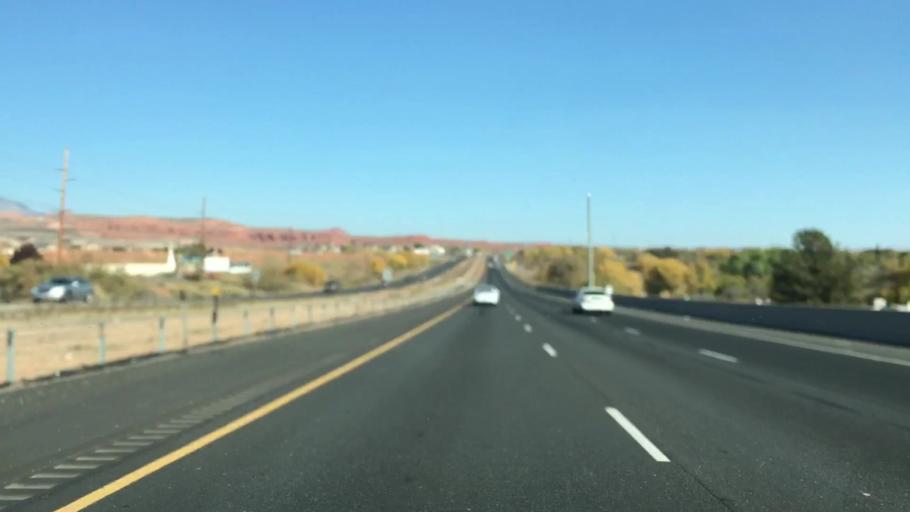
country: US
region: Utah
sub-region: Washington County
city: Washington
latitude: 37.1318
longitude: -113.5201
